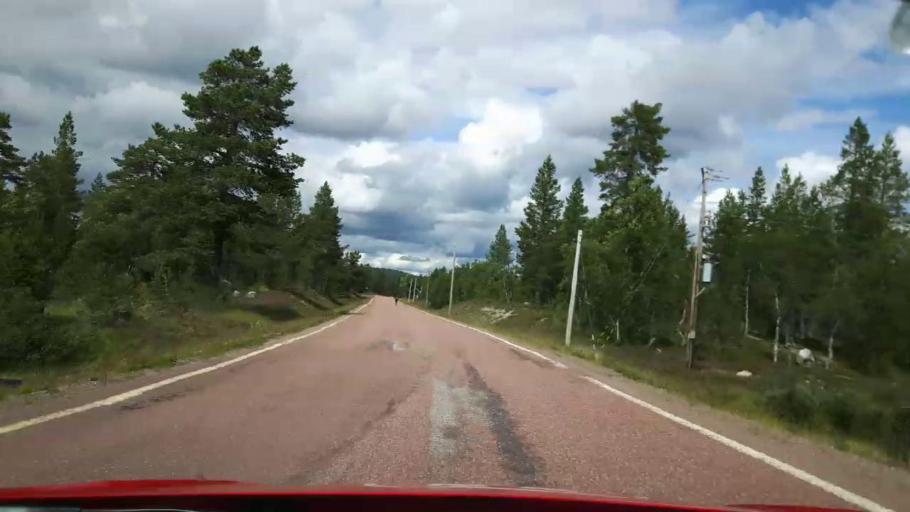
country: NO
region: Hedmark
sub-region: Trysil
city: Innbygda
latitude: 62.0927
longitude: 12.9742
